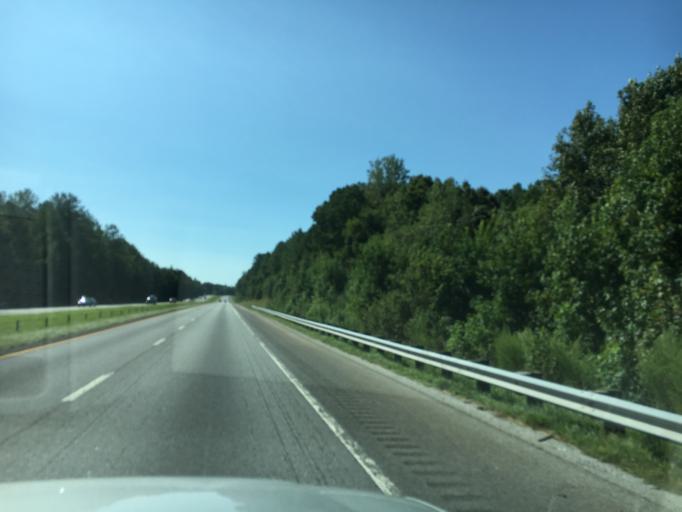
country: US
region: South Carolina
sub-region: Spartanburg County
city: Woodruff
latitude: 34.7852
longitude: -81.9552
